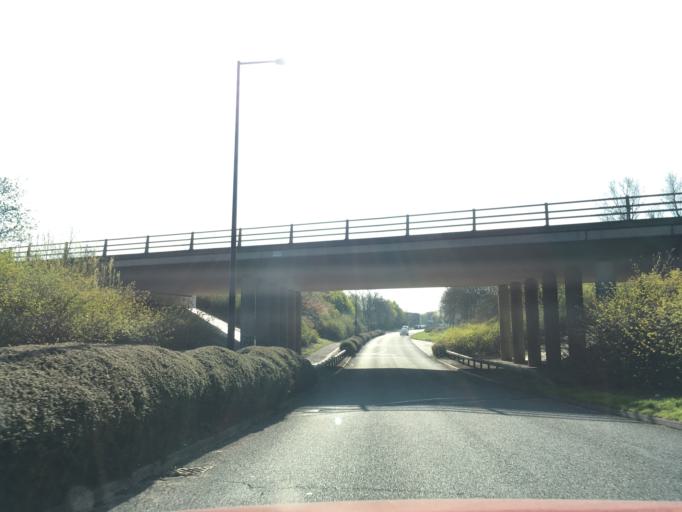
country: GB
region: England
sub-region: Milton Keynes
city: Newport Pagnell
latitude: 52.0698
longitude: -0.7340
